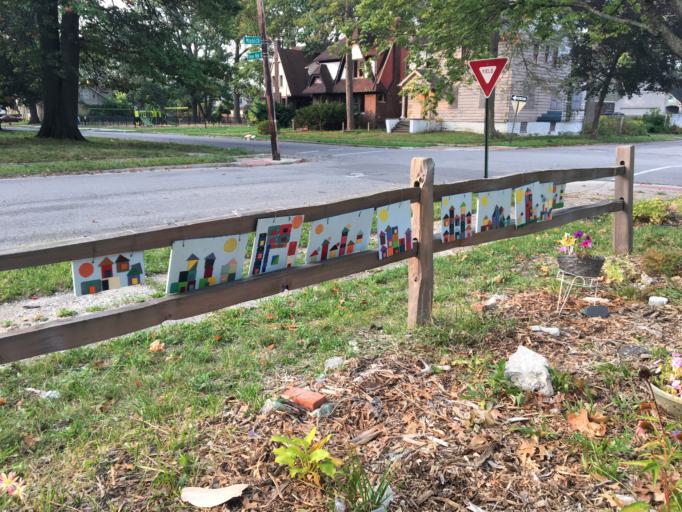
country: US
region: Michigan
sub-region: Wayne County
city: Grosse Pointe Park
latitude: 42.3993
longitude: -82.9376
